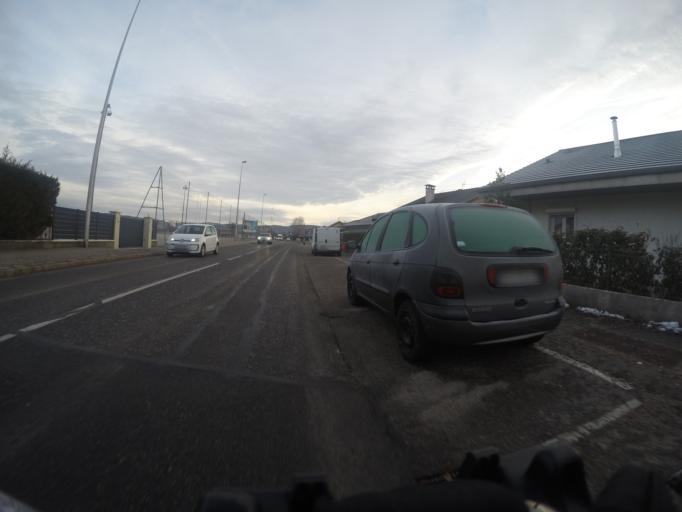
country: FR
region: Rhone-Alpes
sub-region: Departement de la Haute-Savoie
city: Meythet
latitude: 45.9222
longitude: 6.0994
